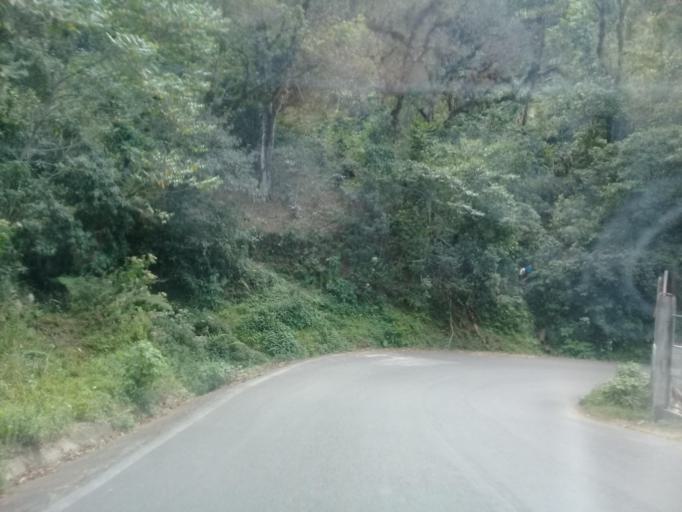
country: MX
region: Veracruz
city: Jalapilla
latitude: 18.8134
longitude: -97.0597
